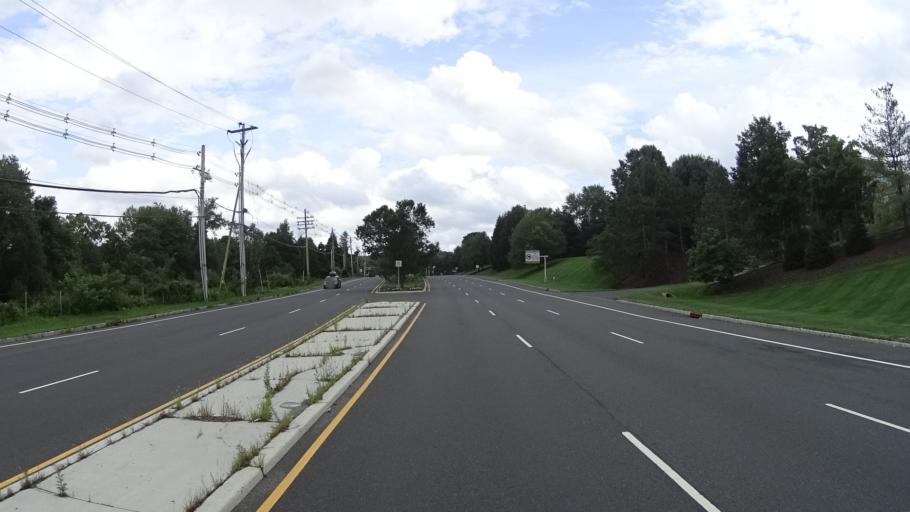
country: US
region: New Jersey
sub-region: Somerset County
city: Warren Township
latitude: 40.6466
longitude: -74.5213
